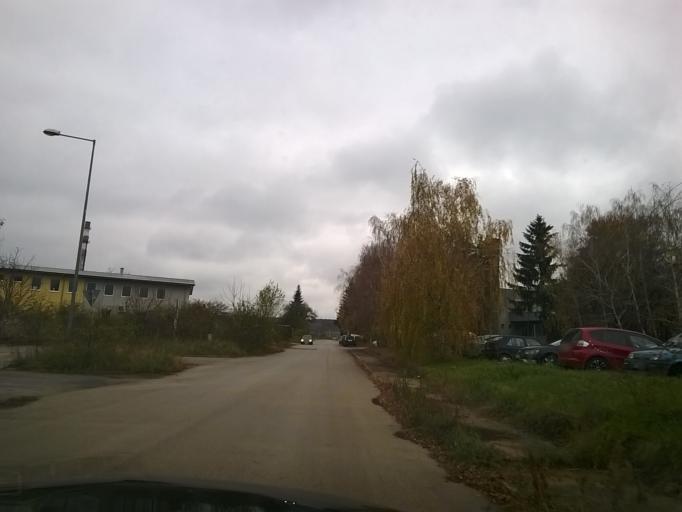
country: SK
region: Nitriansky
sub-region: Okres Nitra
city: Nitra
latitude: 48.2701
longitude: 18.0859
